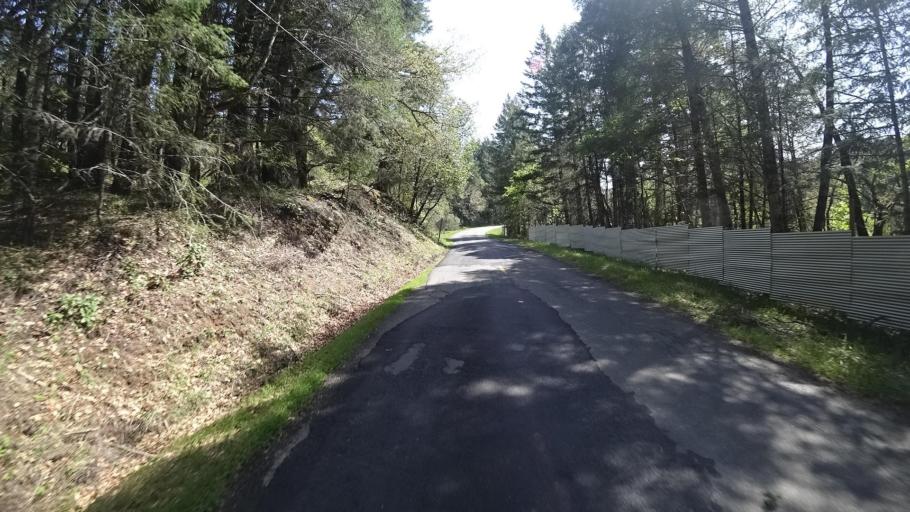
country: US
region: California
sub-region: Humboldt County
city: Redway
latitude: 40.3086
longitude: -123.6546
